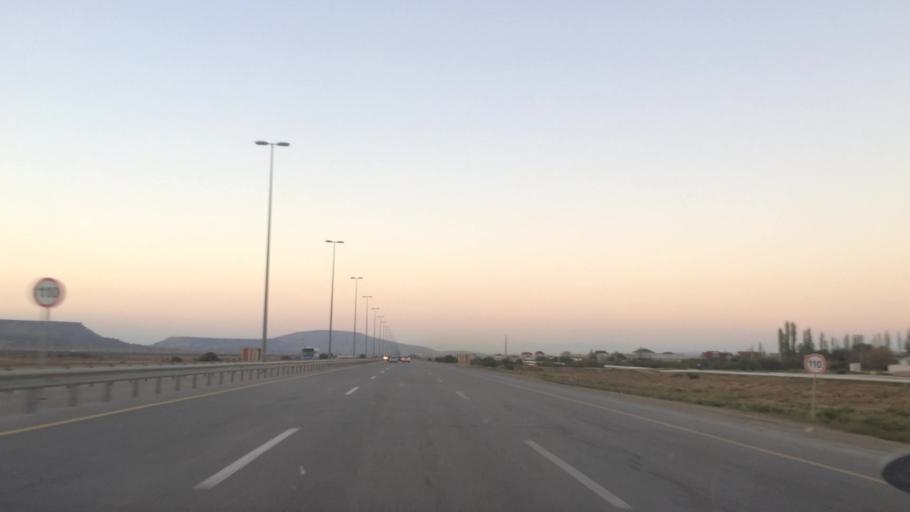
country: AZ
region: Baki
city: Qobustan
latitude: 40.0227
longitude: 49.4245
